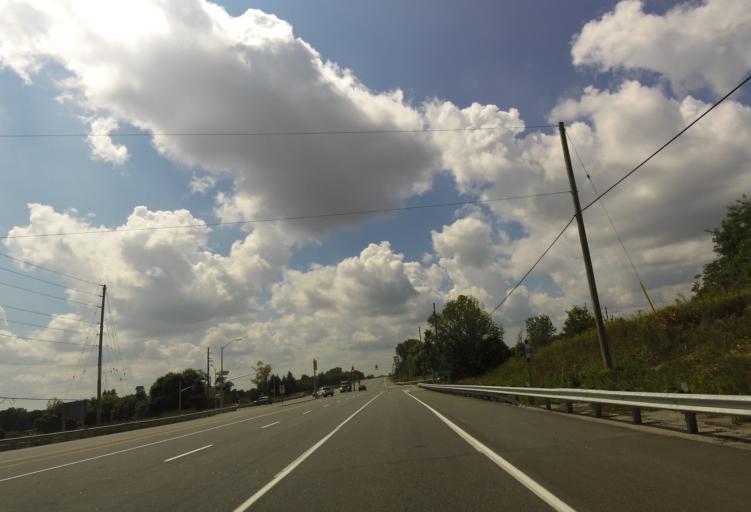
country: CA
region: Ontario
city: Ajax
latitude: 43.9407
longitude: -79.0149
